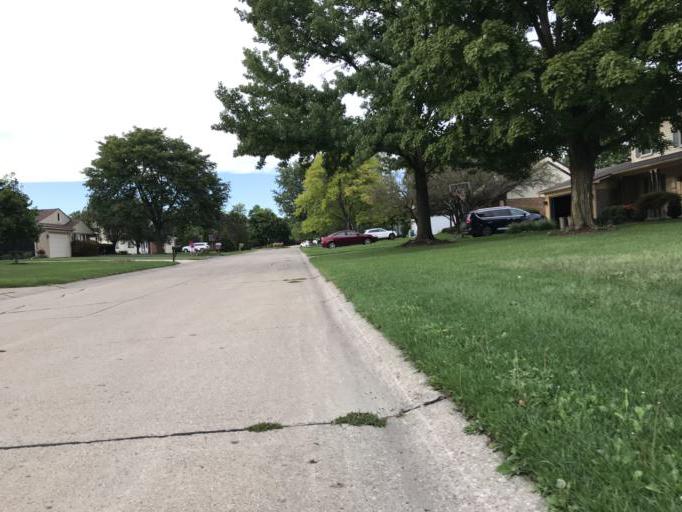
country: US
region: Michigan
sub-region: Oakland County
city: Franklin
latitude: 42.4822
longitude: -83.3242
